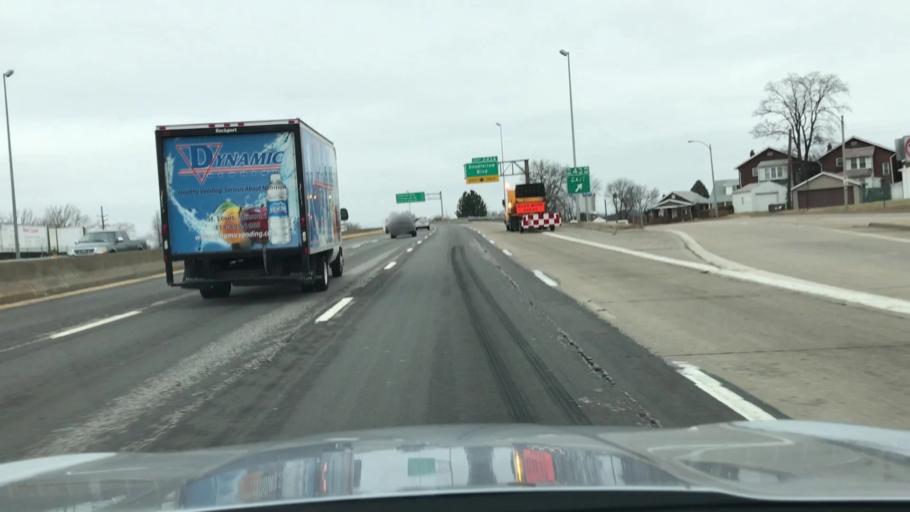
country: US
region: Missouri
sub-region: Saint Louis County
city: Pine Lawn
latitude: 38.6955
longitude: -90.2605
